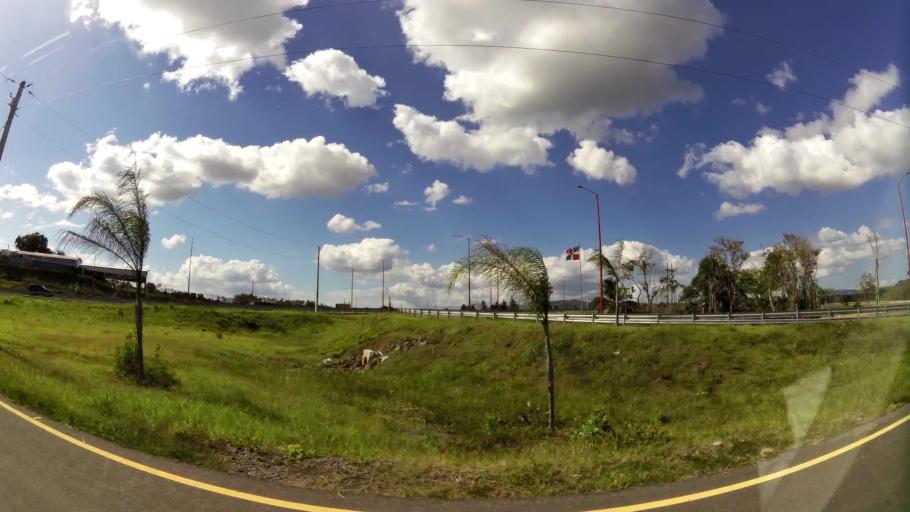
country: DO
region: Santo Domingo
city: Santo Domingo Oeste
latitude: 18.5610
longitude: -70.0687
